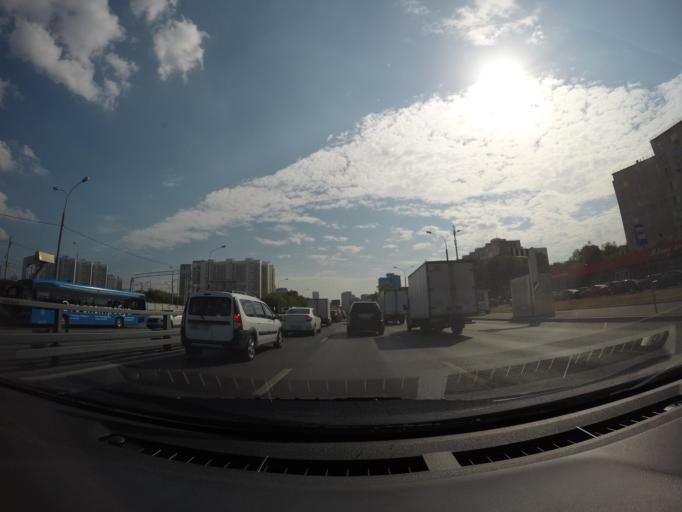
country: RU
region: Moscow
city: Likhobory
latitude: 55.8331
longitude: 37.5727
